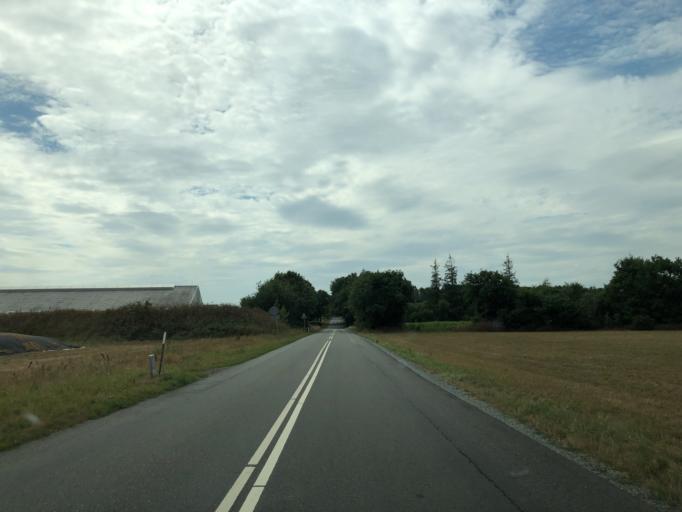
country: DK
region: South Denmark
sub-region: Vejle Kommune
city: Egtved
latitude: 55.6173
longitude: 9.1914
